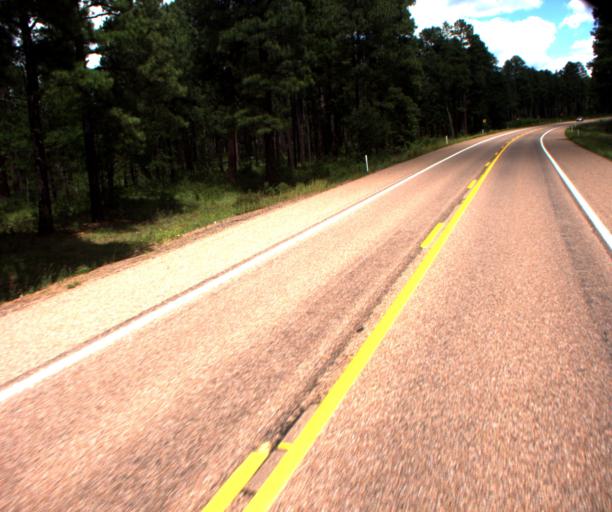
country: US
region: Arizona
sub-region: Navajo County
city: Pinetop-Lakeside
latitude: 34.0785
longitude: -109.8210
